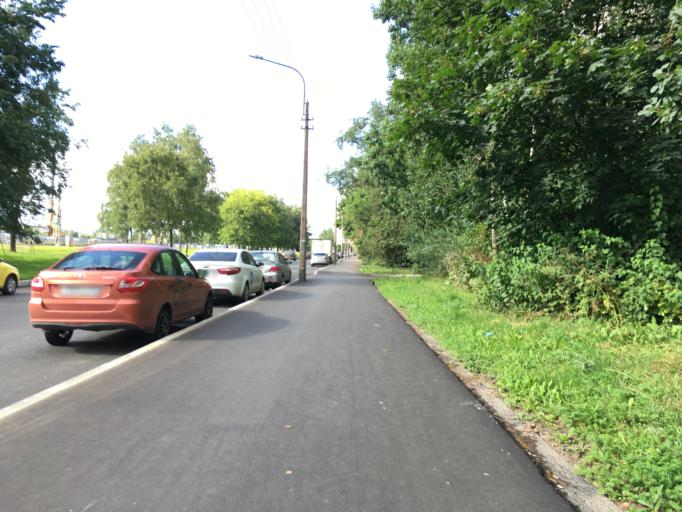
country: RU
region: St.-Petersburg
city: Obukhovo
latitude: 59.8964
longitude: 30.4625
